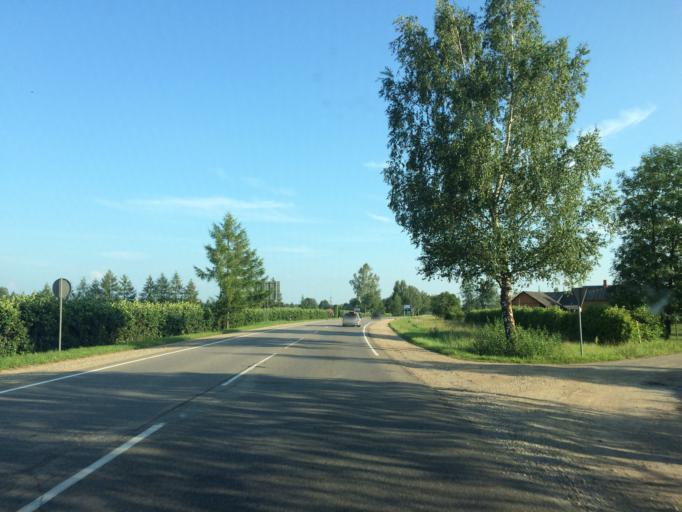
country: LV
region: Plavinu
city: Plavinas
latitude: 56.6136
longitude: 25.7843
